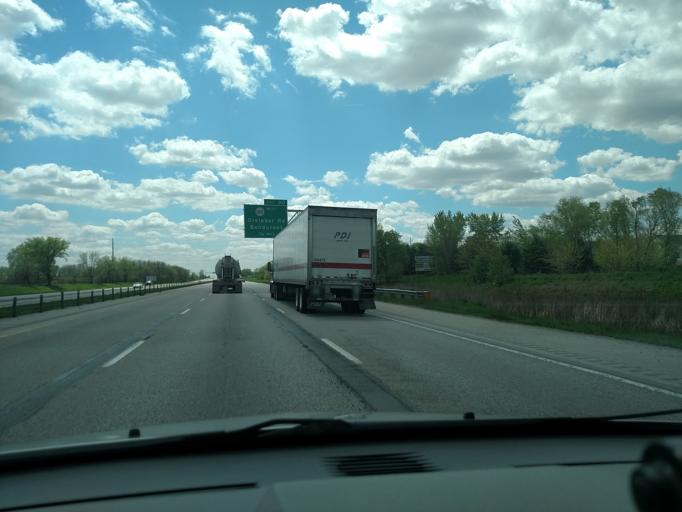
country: US
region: Iowa
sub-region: Polk County
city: Ankeny
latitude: 41.7203
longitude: -93.5767
